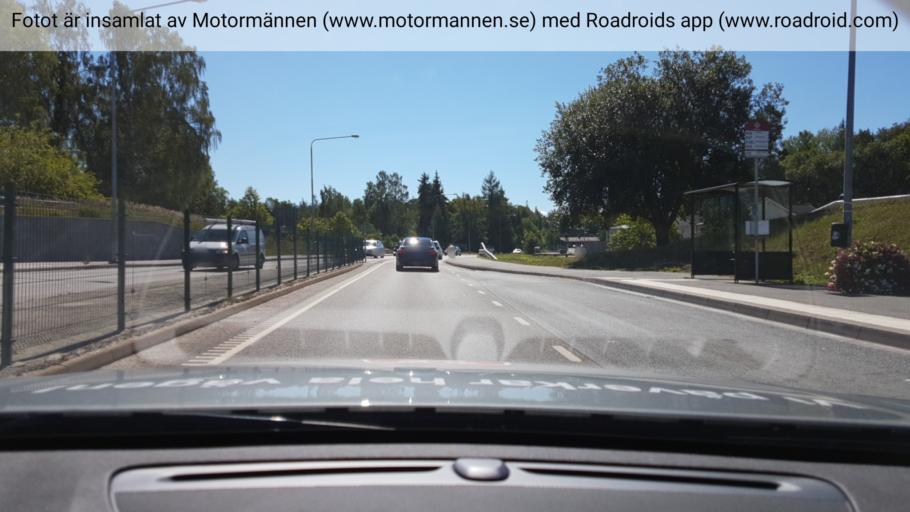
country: SE
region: Stockholm
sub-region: Tyreso Kommun
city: Bollmora
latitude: 59.2137
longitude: 18.2082
